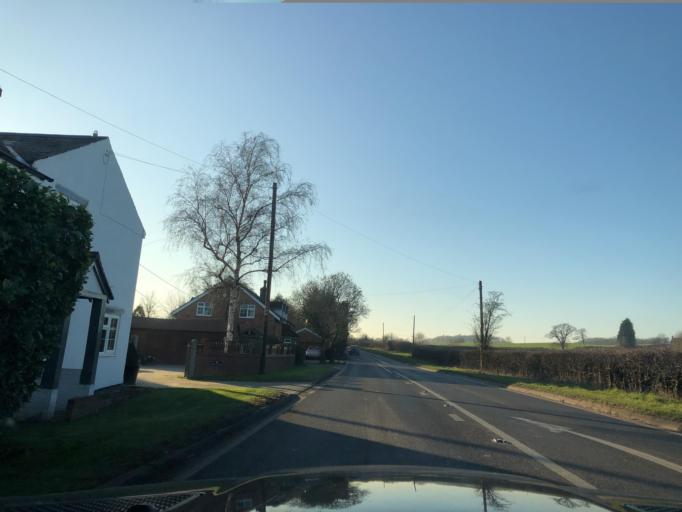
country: GB
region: England
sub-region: Warwickshire
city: Warwick
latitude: 52.2734
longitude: -1.6418
